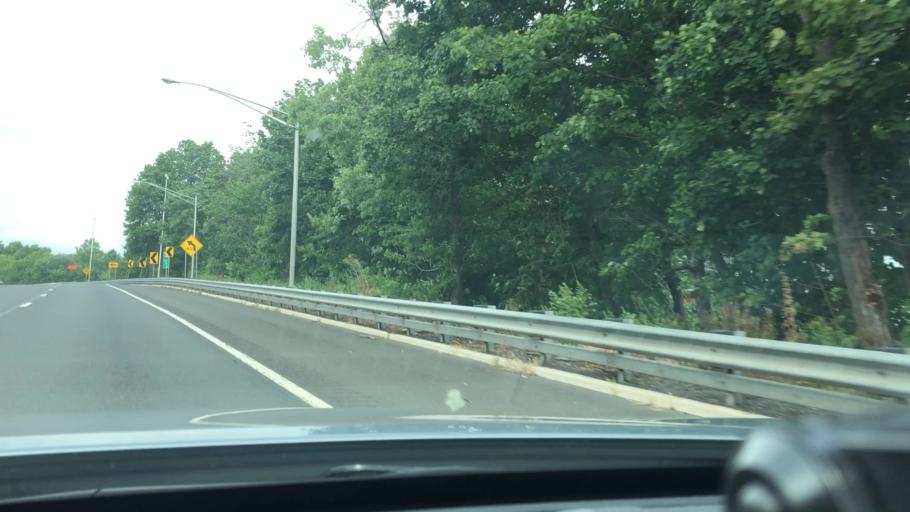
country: US
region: New Jersey
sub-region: Union County
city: Linden
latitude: 40.6415
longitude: -74.2277
